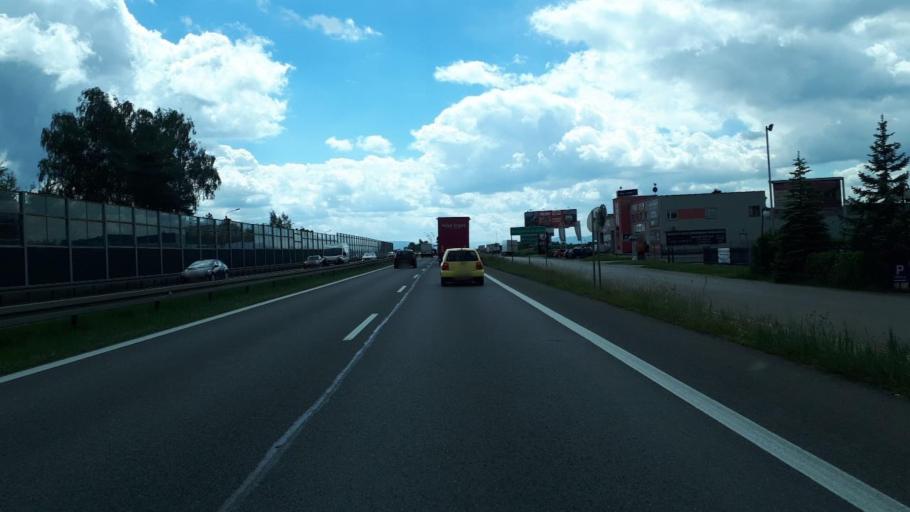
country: PL
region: Silesian Voivodeship
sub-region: Powiat pszczynski
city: Goczalkowice Zdroj
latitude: 49.9612
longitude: 18.9635
